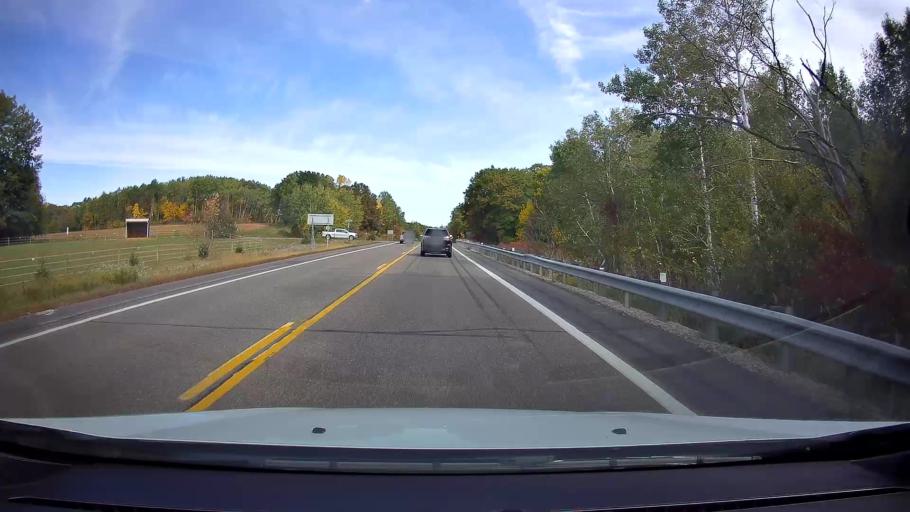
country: US
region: Minnesota
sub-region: Washington County
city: Scandia
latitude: 45.2954
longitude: -92.7687
